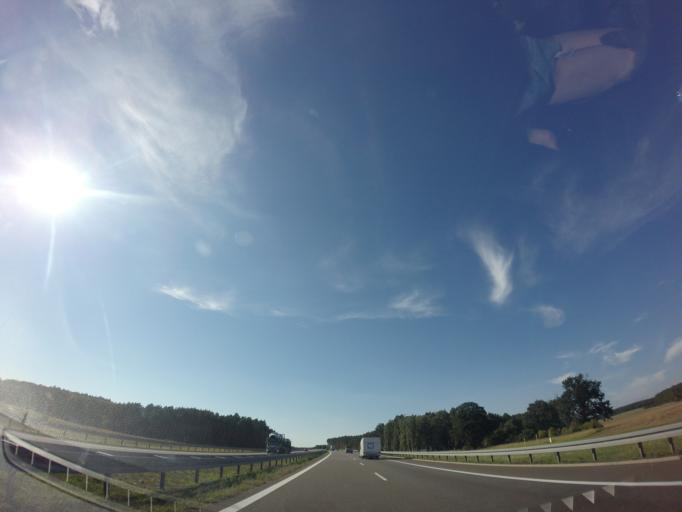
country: PL
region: Lubusz
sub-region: Powiat swiebodzinski
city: Swiebodzin
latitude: 52.1964
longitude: 15.5784
